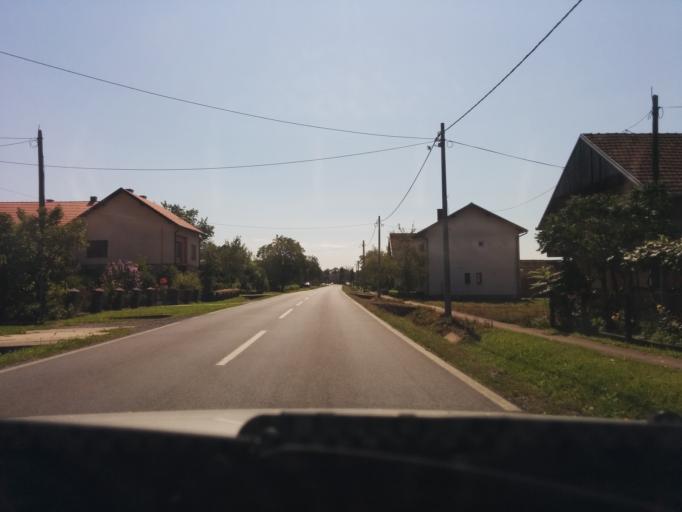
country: HR
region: Sisacko-Moslavacka
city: Lipovljani
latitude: 45.3675
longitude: 16.9316
